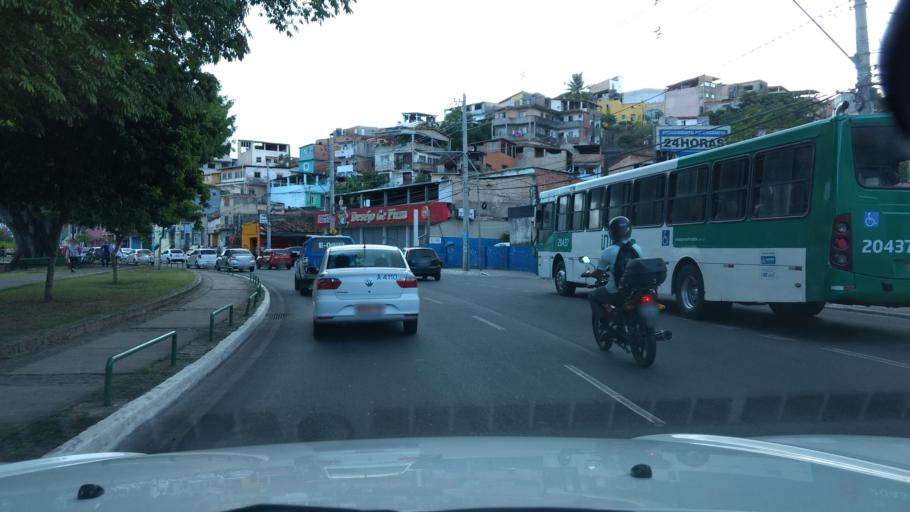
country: BR
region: Bahia
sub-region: Salvador
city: Salvador
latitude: -12.9850
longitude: -38.5041
